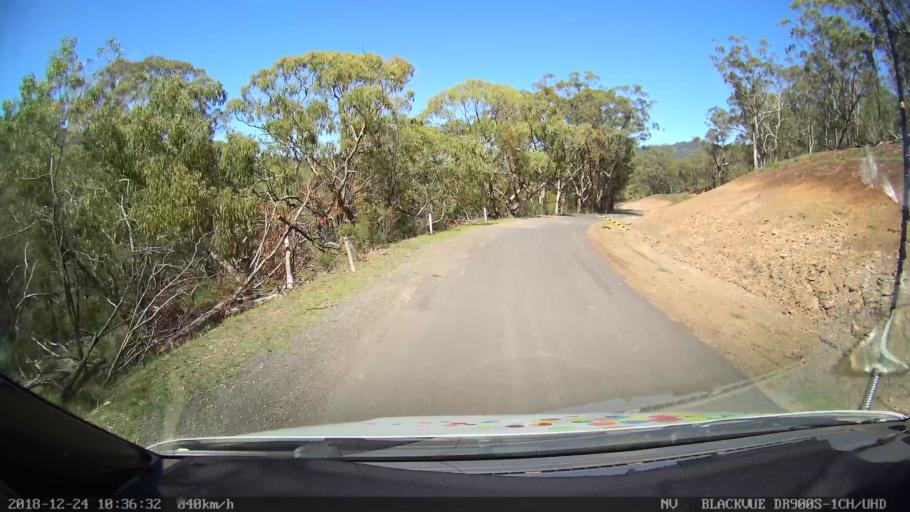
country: AU
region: New South Wales
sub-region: Upper Hunter Shire
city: Merriwa
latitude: -31.8448
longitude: 150.4994
